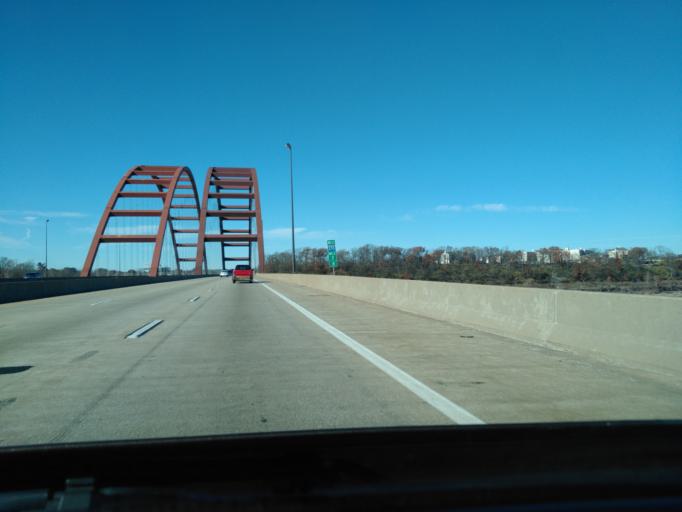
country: US
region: Missouri
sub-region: Saint Louis County
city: Oakville
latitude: 38.4862
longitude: -90.2736
